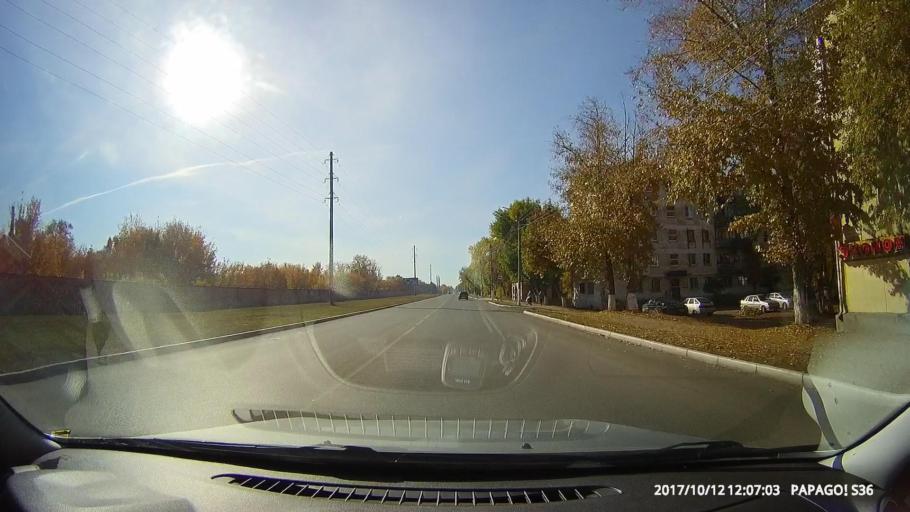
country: RU
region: Samara
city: Chapayevsk
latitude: 52.9693
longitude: 49.7036
